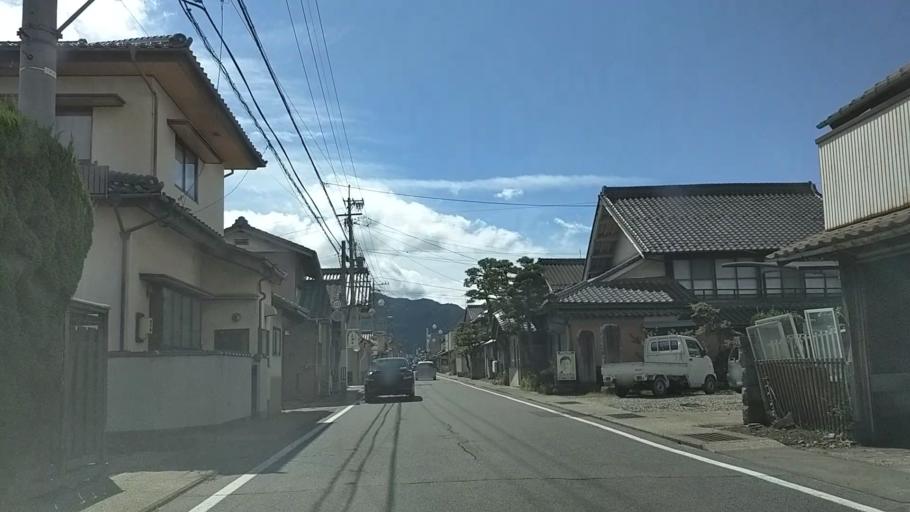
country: JP
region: Nagano
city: Suzaka
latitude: 36.6243
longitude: 138.2574
